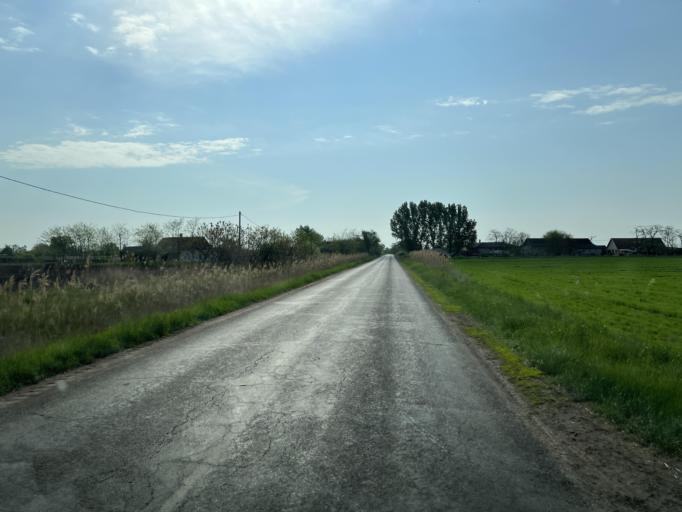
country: HU
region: Pest
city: Jaszkarajeno
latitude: 47.0463
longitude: 20.0858
